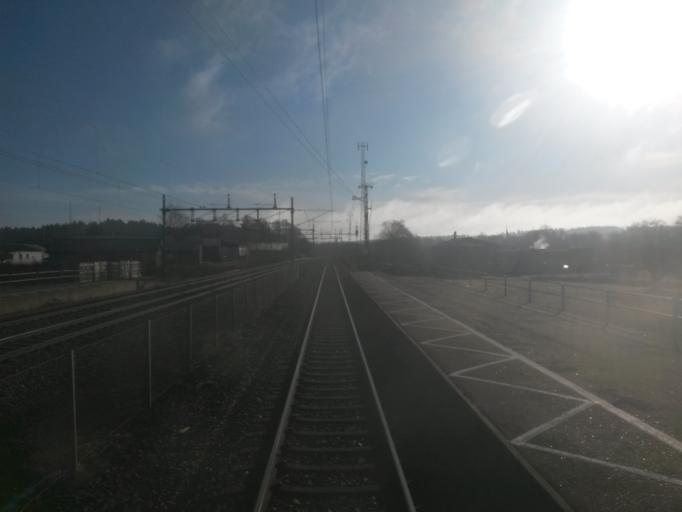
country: SE
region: Vaestra Goetaland
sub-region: Vargarda Kommun
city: Vargarda
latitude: 58.0312
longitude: 12.8121
